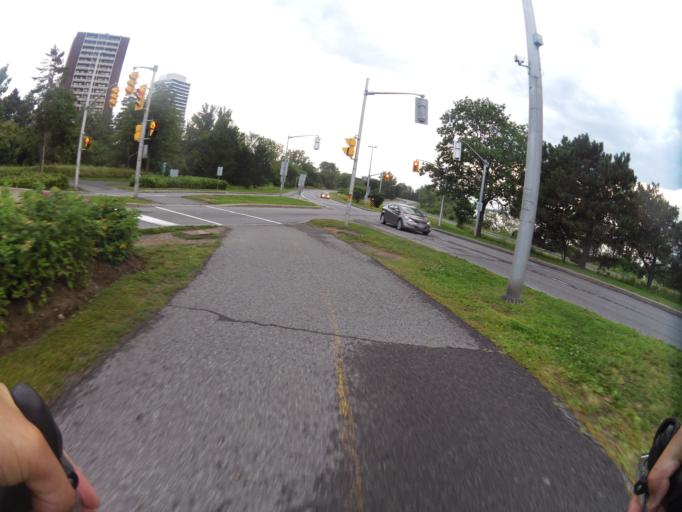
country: CA
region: Ontario
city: Ottawa
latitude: 45.3925
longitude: -75.7608
